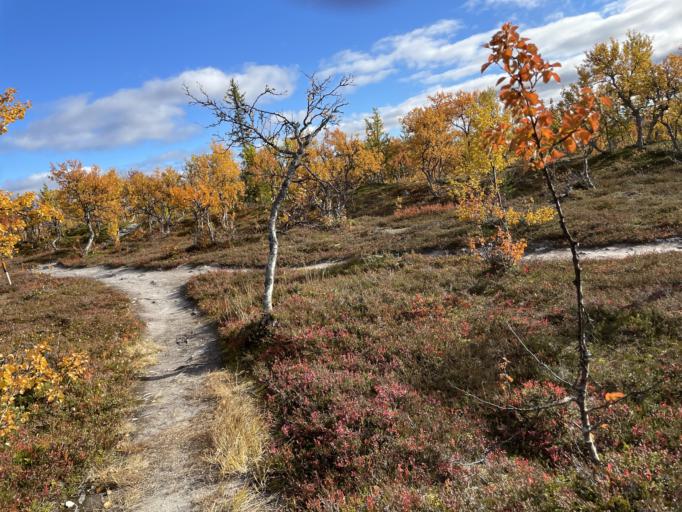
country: SE
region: Jaemtland
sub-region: Are Kommun
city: Are
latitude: 62.6913
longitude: 12.9093
